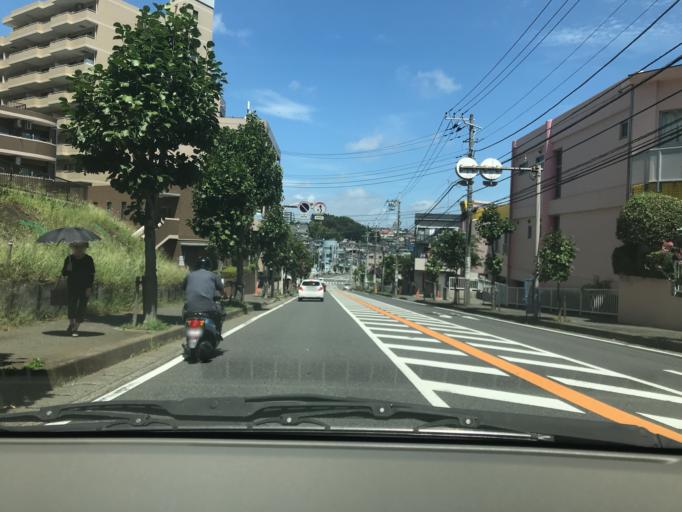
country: JP
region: Kanagawa
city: Fujisawa
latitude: 35.3595
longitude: 139.4679
